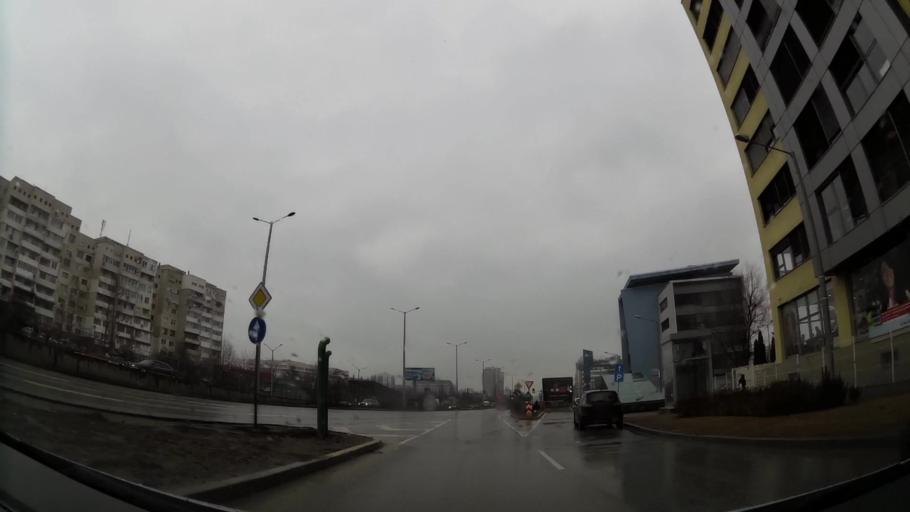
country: BG
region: Sofia-Capital
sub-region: Stolichna Obshtina
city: Sofia
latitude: 42.6285
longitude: 23.3733
